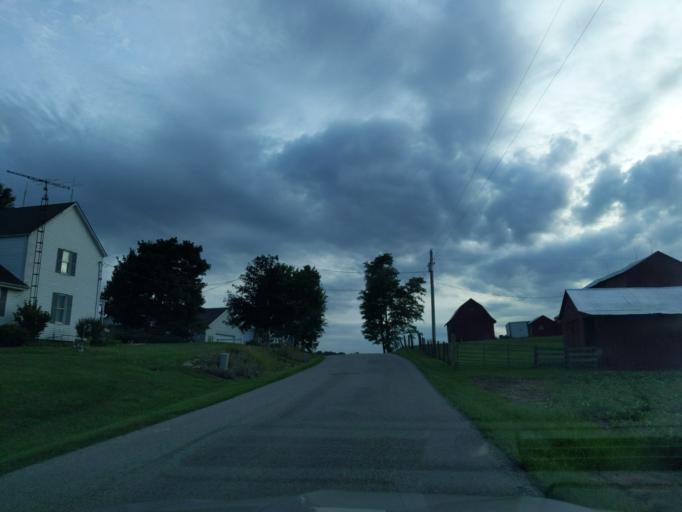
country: US
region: Indiana
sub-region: Ripley County
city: Sunman
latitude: 39.2885
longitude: -85.0967
